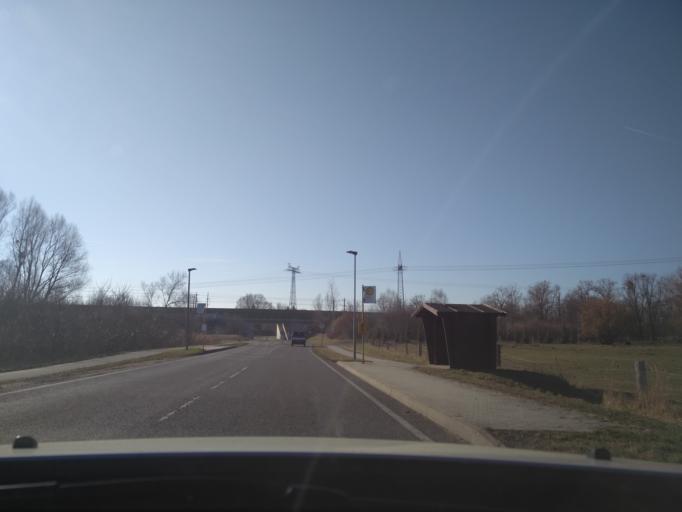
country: DE
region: Brandenburg
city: Wustermark
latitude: 52.5530
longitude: 12.9520
